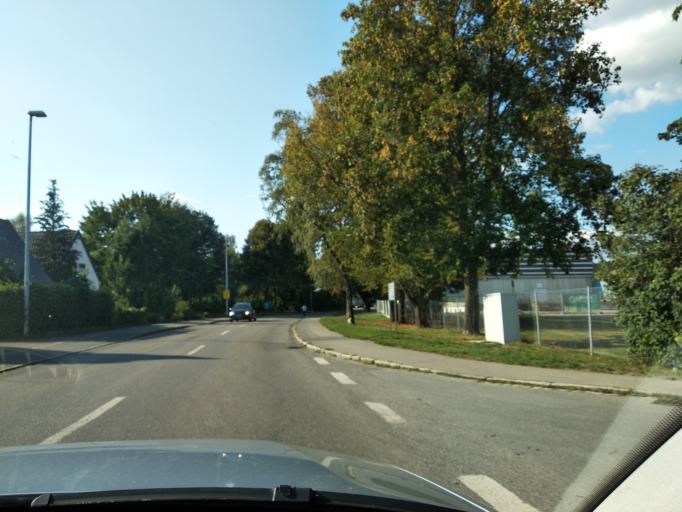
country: DE
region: Baden-Wuerttemberg
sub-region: Tuebingen Region
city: Leutkirch im Allgau
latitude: 47.8335
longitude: 10.0191
